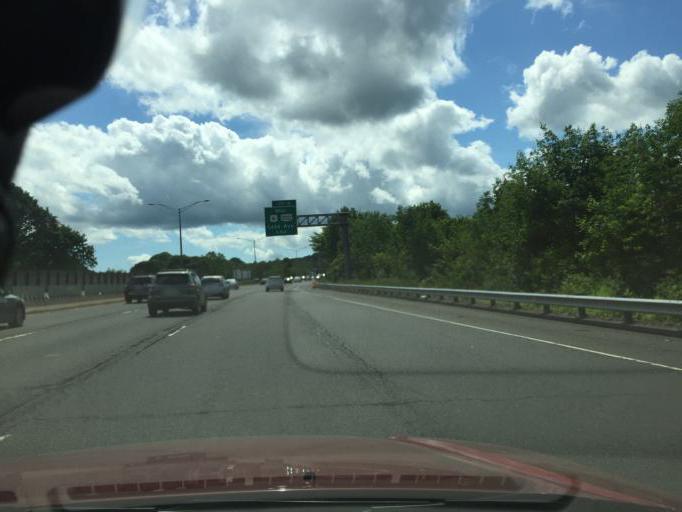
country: US
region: Connecticut
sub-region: Fairfield County
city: Danbury
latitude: 41.4025
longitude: -73.4649
